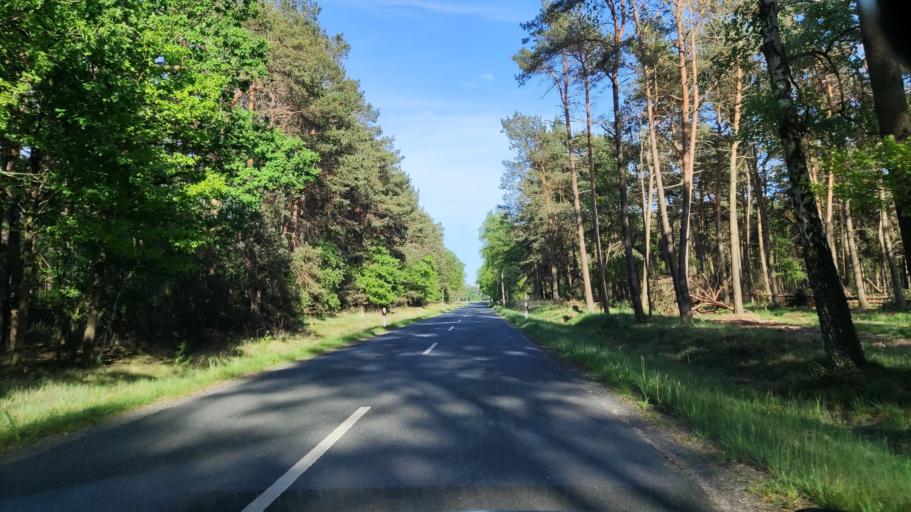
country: DE
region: Lower Saxony
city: Otter
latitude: 53.1817
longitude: 9.7668
